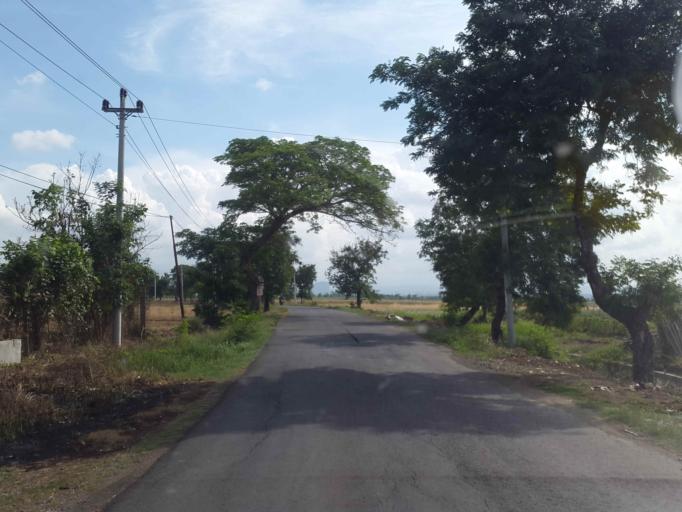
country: ID
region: Central Java
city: Pemalang
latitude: -6.8979
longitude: 109.3254
